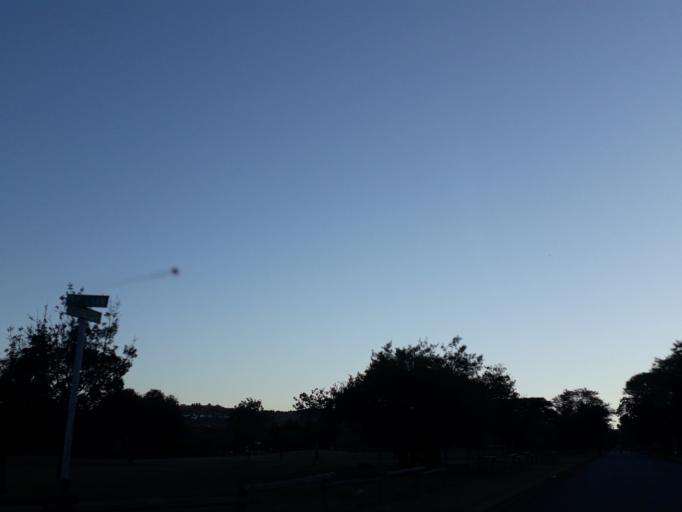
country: ZA
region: Gauteng
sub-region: City of Johannesburg Metropolitan Municipality
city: Roodepoort
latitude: -26.1302
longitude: 27.9429
